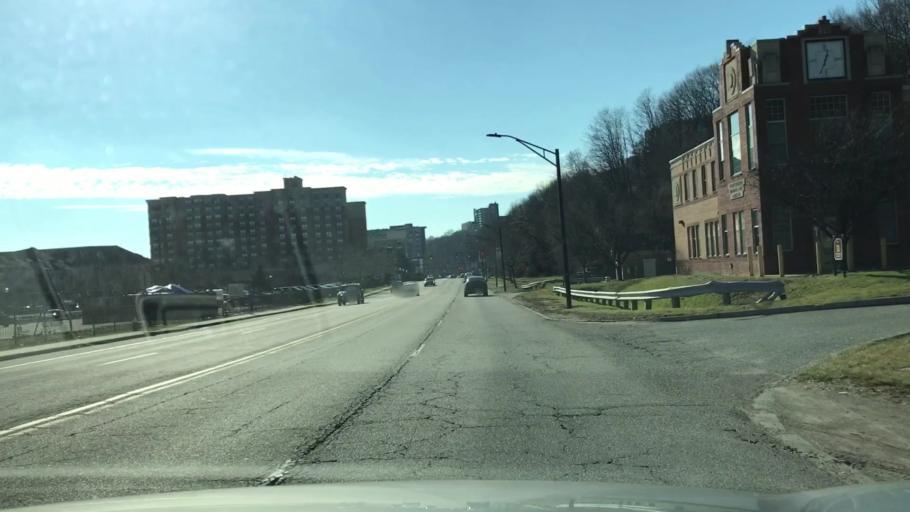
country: US
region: New Jersey
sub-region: Hudson County
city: West New York
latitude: 40.7821
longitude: -74.0076
